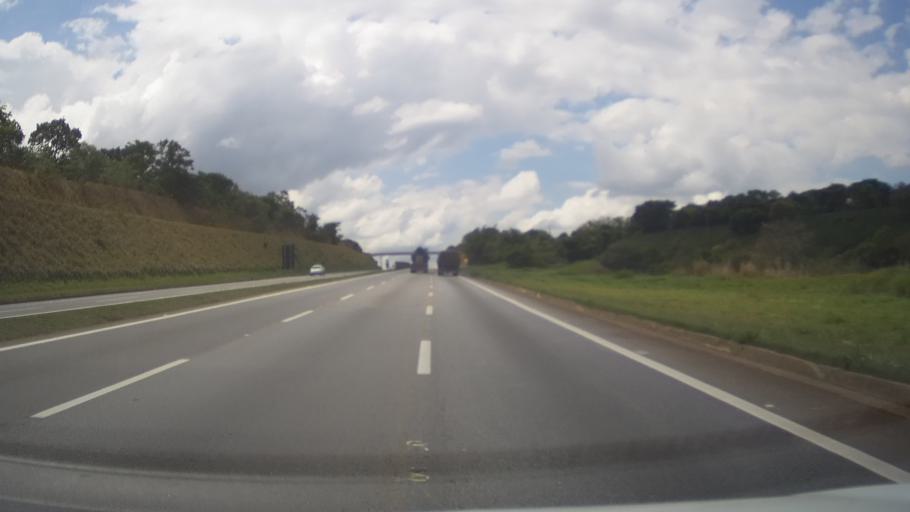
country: BR
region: Minas Gerais
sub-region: Nepomuceno
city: Nepomuceno
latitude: -21.2834
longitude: -45.1400
